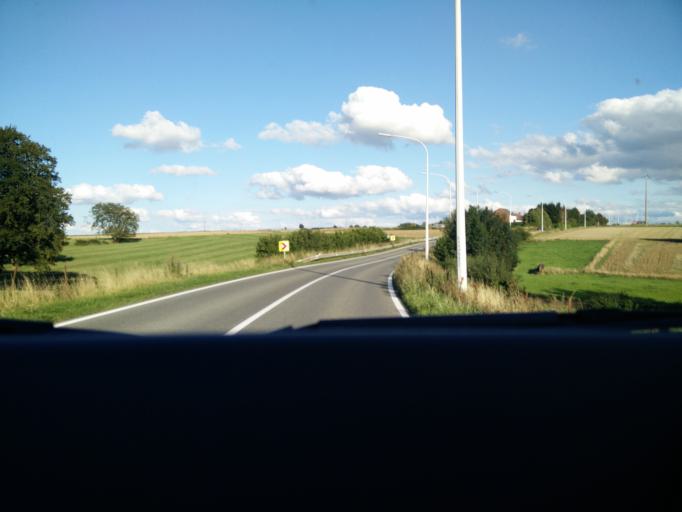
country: BE
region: Wallonia
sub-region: Province du Hainaut
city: Beaumont
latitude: 50.2380
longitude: 4.2571
